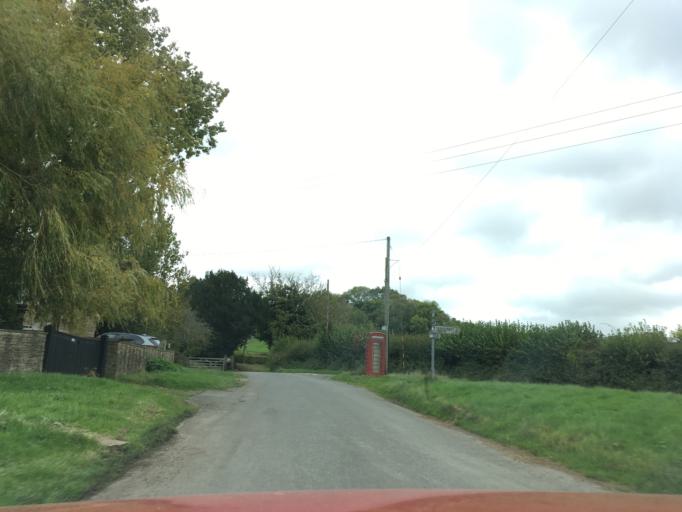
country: GB
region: England
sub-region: South Gloucestershire
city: Horton
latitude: 51.5887
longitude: -2.3454
